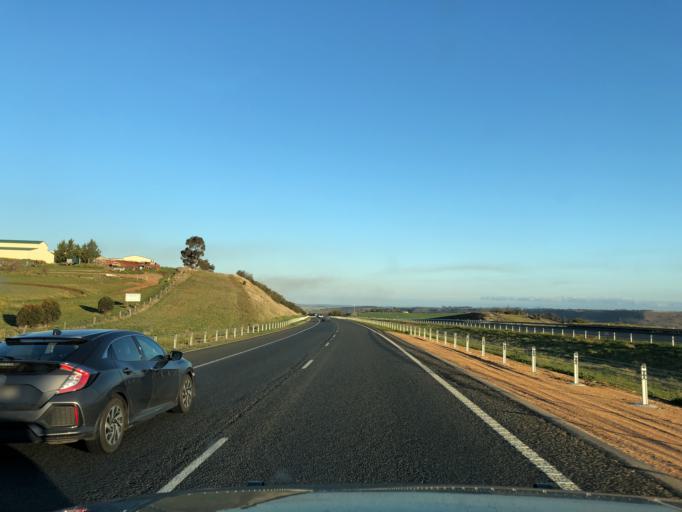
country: AU
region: Victoria
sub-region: Moorabool
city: Bacchus Marsh
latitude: -37.6517
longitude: 144.3684
